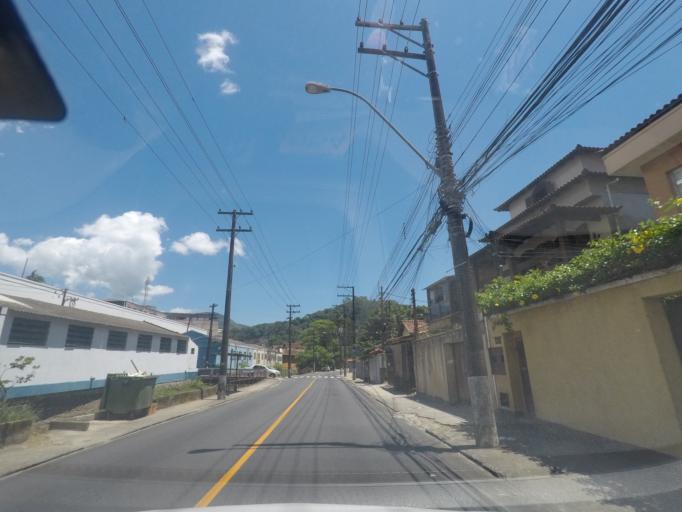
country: BR
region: Rio de Janeiro
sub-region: Petropolis
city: Petropolis
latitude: -22.5183
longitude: -43.1689
